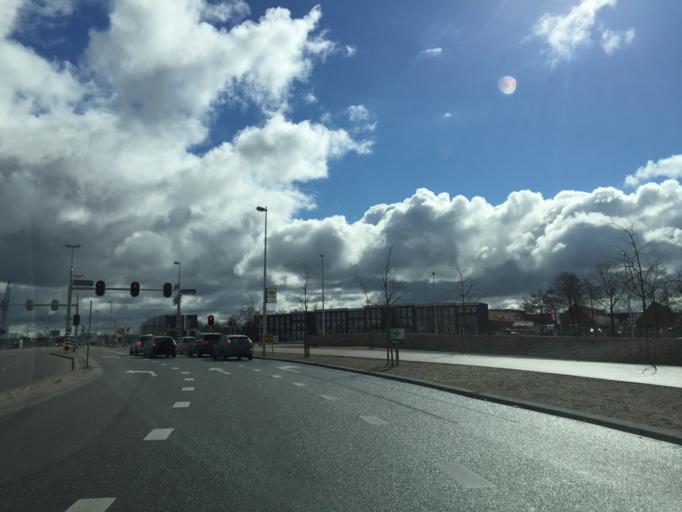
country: NL
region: Utrecht
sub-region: Stichtse Vecht
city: Maarssen
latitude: 52.0991
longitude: 5.0607
